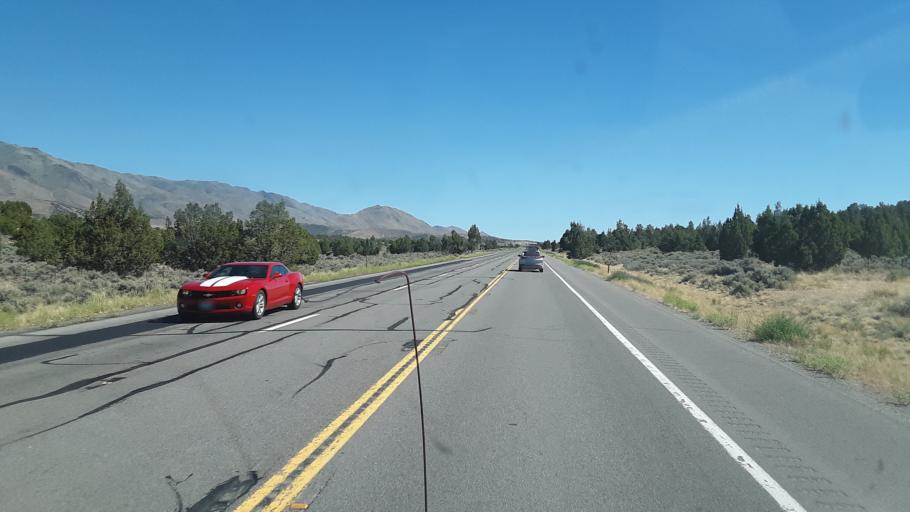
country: US
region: Nevada
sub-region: Washoe County
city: Cold Springs
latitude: 39.8414
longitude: -120.0398
